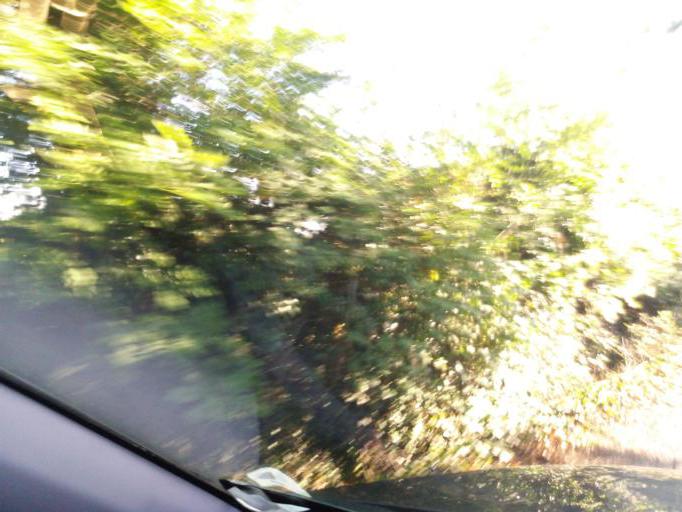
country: IE
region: Leinster
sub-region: Dublin City
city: Finglas
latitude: 53.4574
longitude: -6.3173
